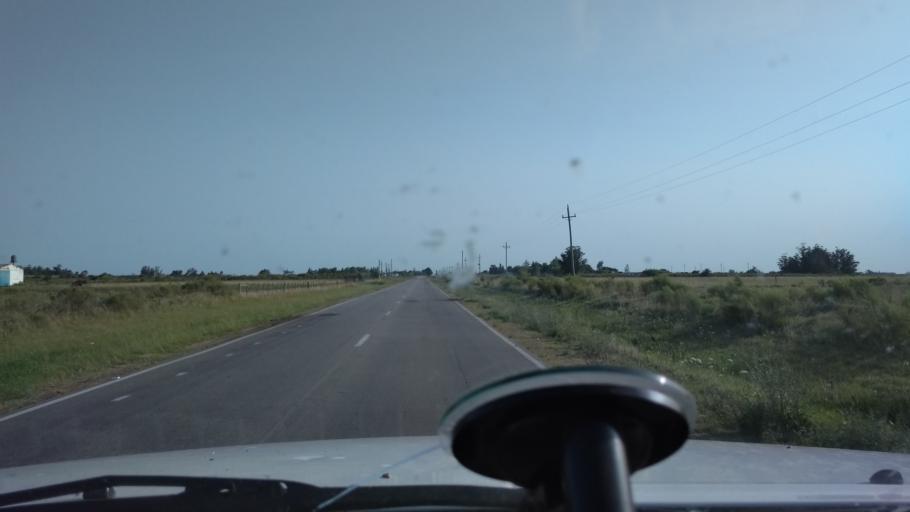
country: UY
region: Canelones
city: Santa Rosa
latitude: -34.5145
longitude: -56.0542
